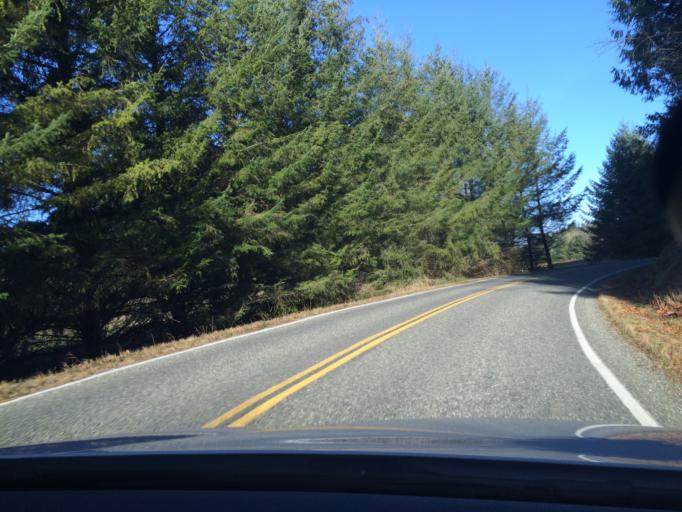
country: US
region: Washington
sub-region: Whatcom County
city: Everson
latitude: 48.8505
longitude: -122.4011
